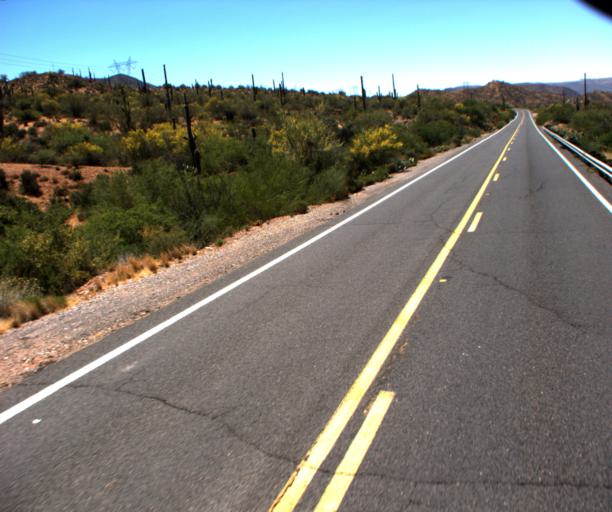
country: US
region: Arizona
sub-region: Pinal County
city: Superior
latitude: 33.1904
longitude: -111.0444
